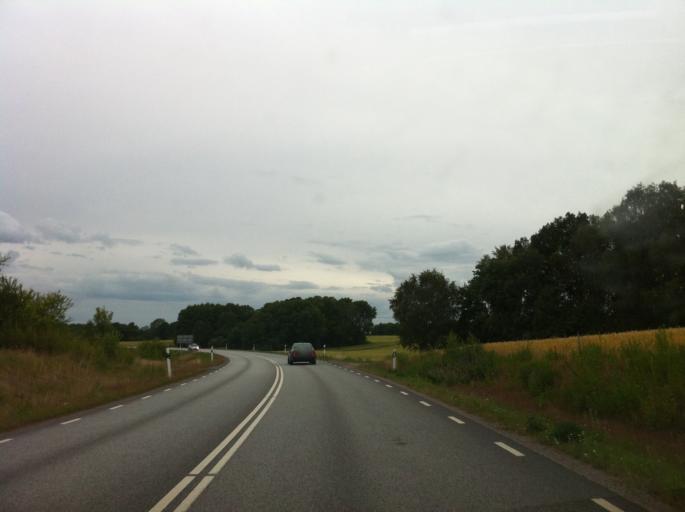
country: SE
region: Skane
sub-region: Hoors Kommun
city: Hoeoer
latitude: 55.9409
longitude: 13.5453
